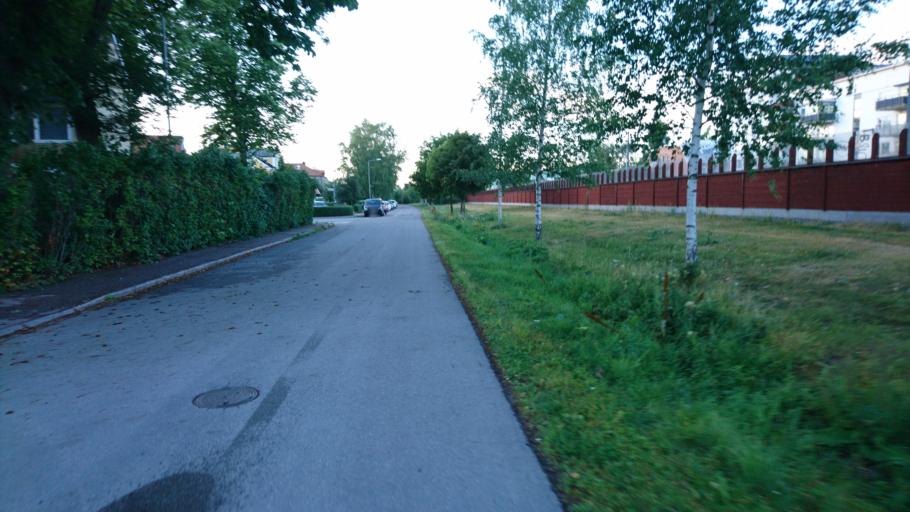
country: SE
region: Uppsala
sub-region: Uppsala Kommun
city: Uppsala
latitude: 59.8672
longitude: 17.6354
